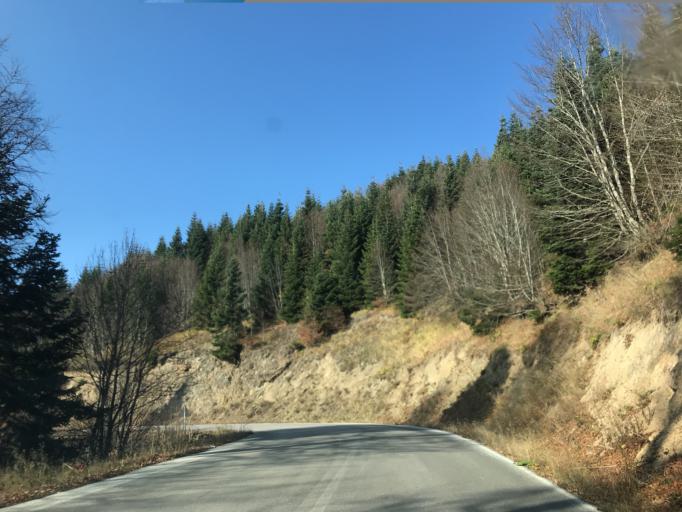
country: TR
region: Bolu
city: Bolu
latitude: 40.8863
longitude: 31.6819
